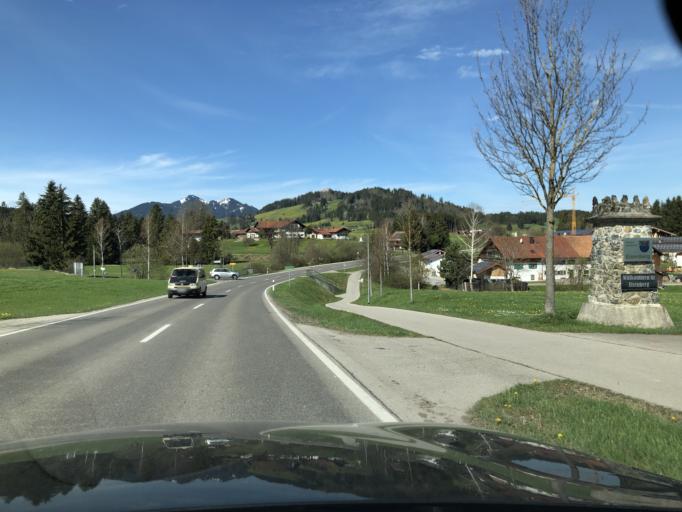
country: DE
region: Bavaria
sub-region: Swabia
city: Hopferau
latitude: 47.6129
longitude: 10.6265
